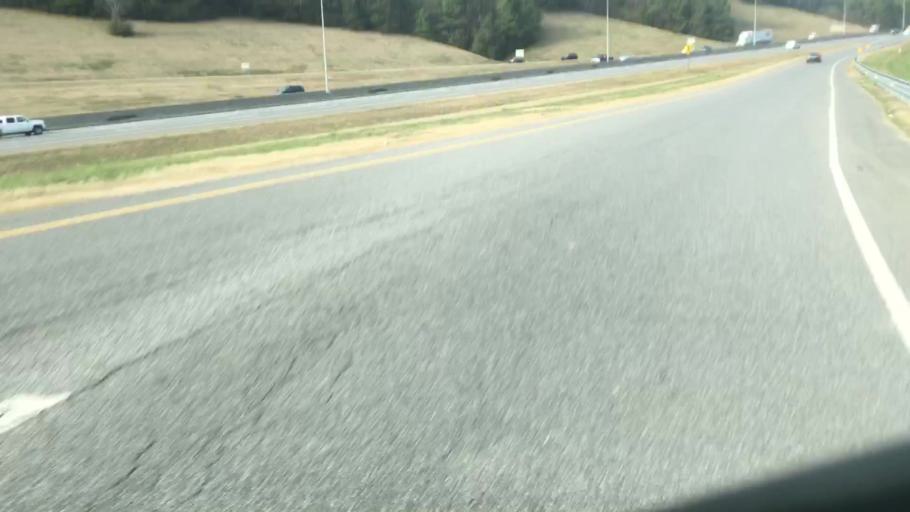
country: US
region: Alabama
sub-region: Jefferson County
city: Cahaba Heights
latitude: 33.4917
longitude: -86.7054
